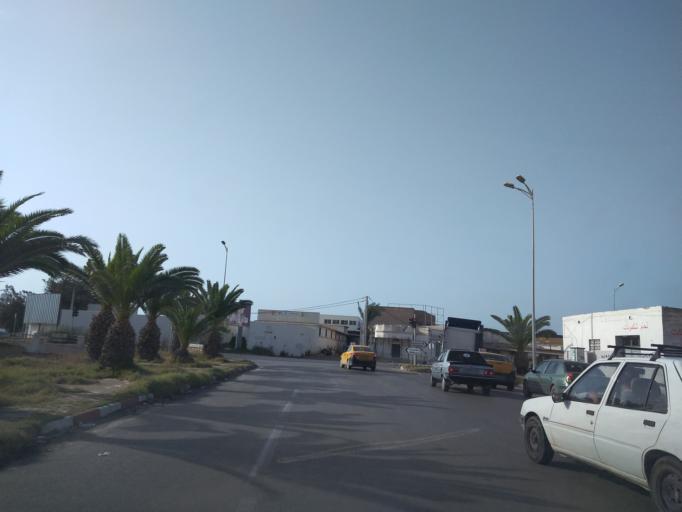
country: TN
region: Safaqis
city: Sfax
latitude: 34.7308
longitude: 10.7465
